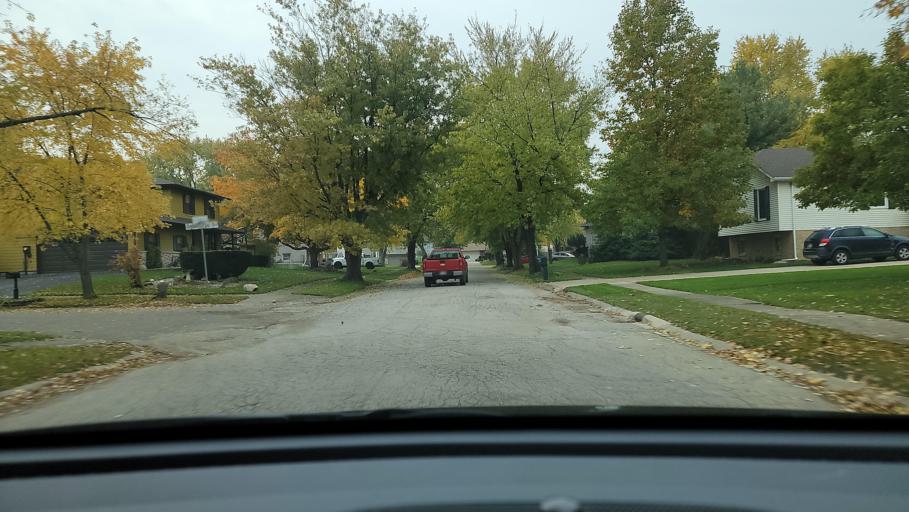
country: US
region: Indiana
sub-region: Porter County
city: Portage
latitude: 41.5596
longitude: -87.1775
